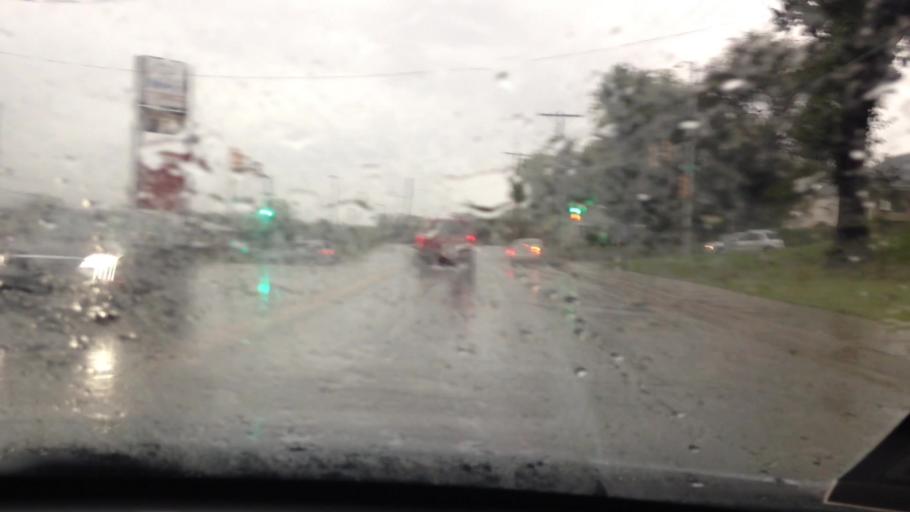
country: US
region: Kansas
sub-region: Leavenworth County
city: Leavenworth
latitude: 39.2882
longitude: -94.9090
